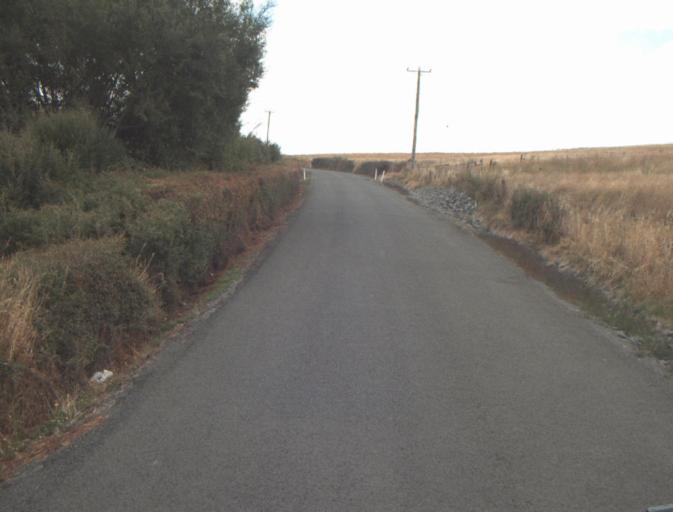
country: AU
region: Tasmania
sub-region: Northern Midlands
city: Evandale
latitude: -41.5241
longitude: 147.2473
